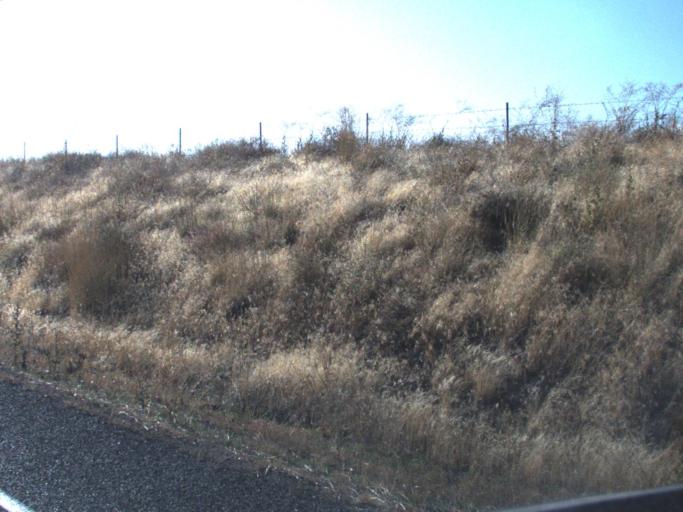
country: US
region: Washington
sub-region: Walla Walla County
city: Burbank
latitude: 46.2731
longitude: -118.7671
